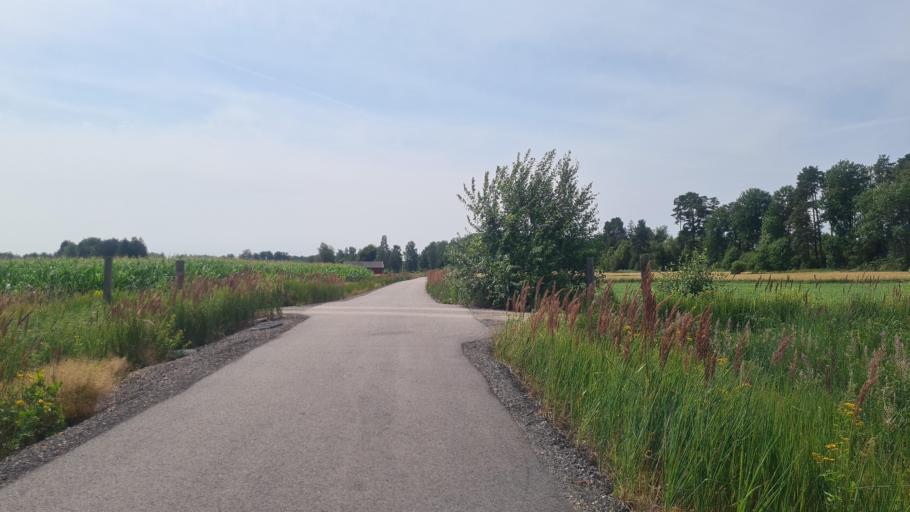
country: SE
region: Kronoberg
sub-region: Ljungby Kommun
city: Lagan
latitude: 56.8977
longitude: 13.9882
